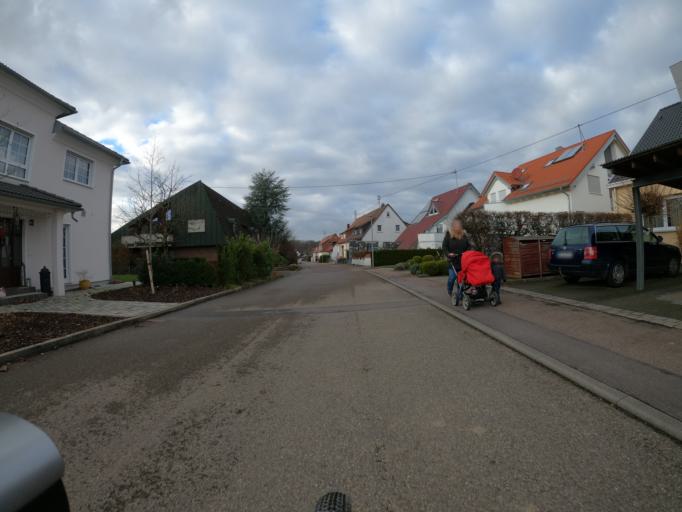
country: DE
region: Baden-Wuerttemberg
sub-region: Regierungsbezirk Stuttgart
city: Notzingen
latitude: 48.6751
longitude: 9.4727
